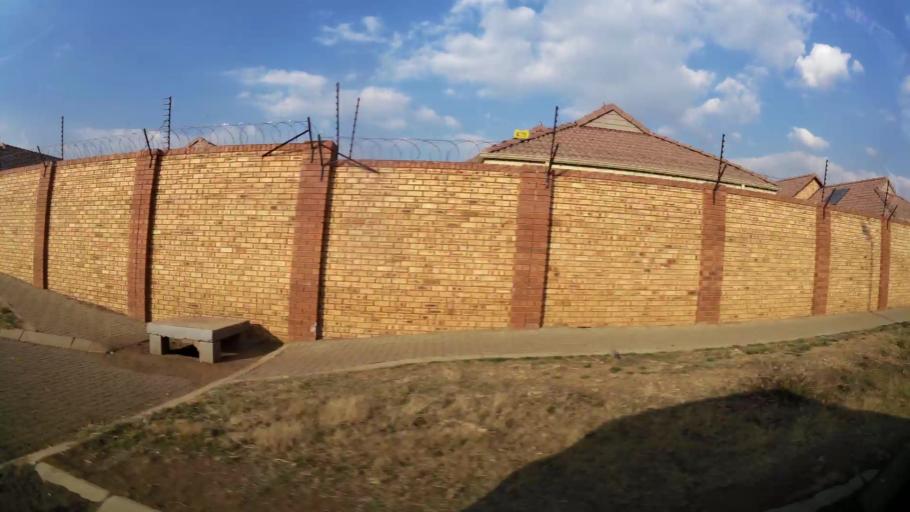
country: ZA
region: Gauteng
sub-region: Ekurhuleni Metropolitan Municipality
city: Benoni
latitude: -26.1137
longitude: 28.2806
